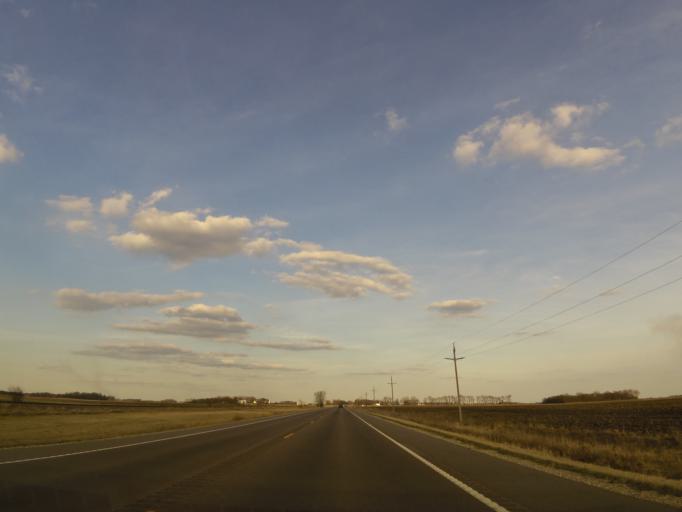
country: US
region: Minnesota
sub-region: McLeod County
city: Hutchinson
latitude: 44.7231
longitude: -94.4473
